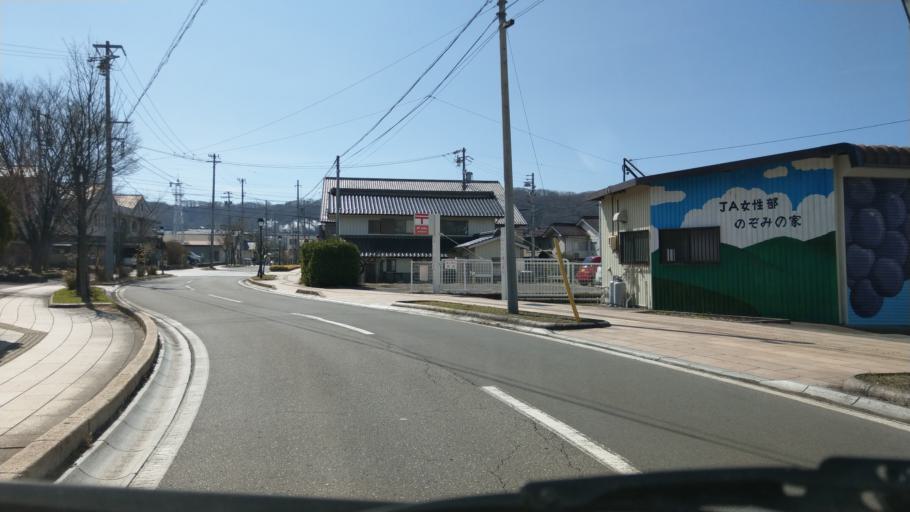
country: JP
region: Nagano
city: Ueda
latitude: 36.3574
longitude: 138.3313
